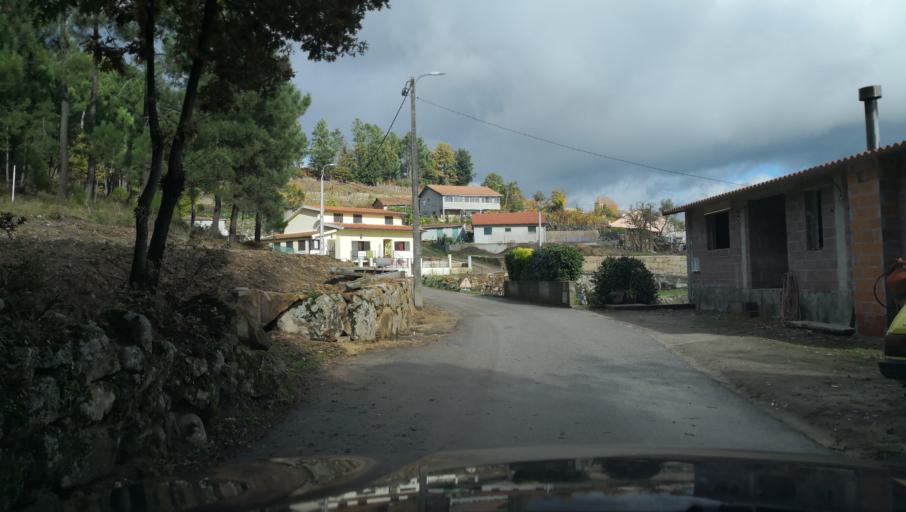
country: PT
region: Vila Real
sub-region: Vila Real
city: Vila Real
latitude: 41.3264
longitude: -7.7551
